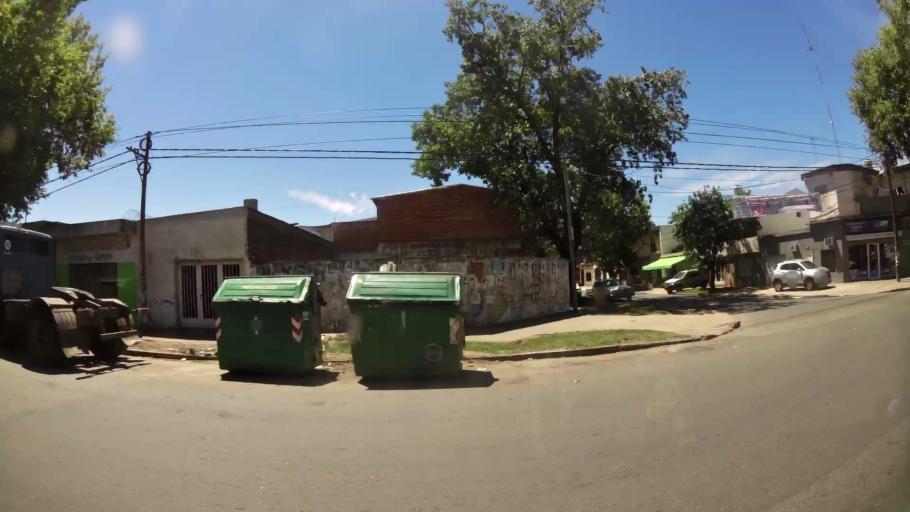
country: AR
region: Santa Fe
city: Perez
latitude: -32.9567
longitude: -60.7118
